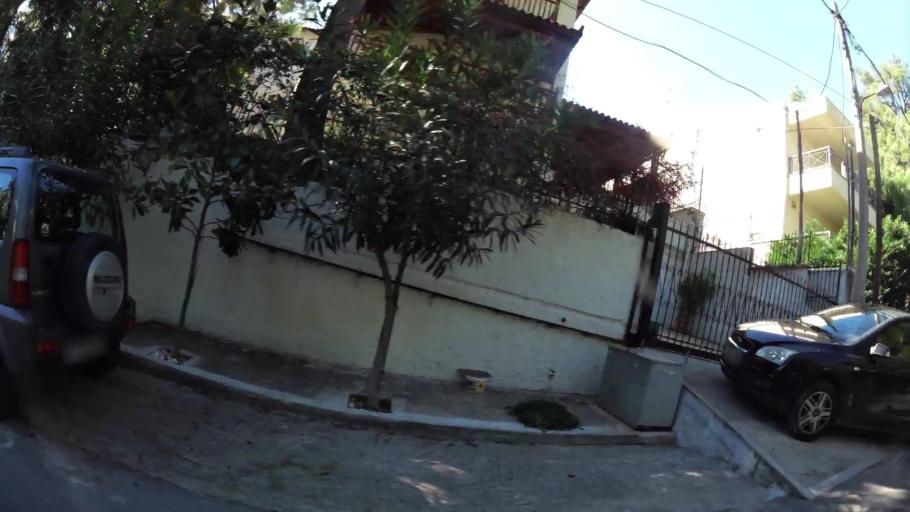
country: GR
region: Attica
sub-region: Nomarchia Anatolikis Attikis
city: Dionysos
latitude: 38.1017
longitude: 23.8880
